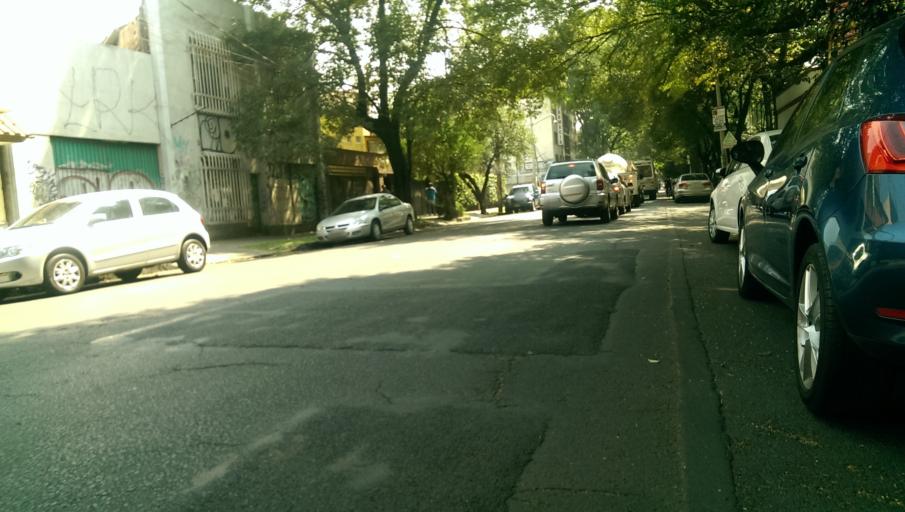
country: MX
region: Mexico City
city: Coyoacan
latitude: 19.3529
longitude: -99.1658
